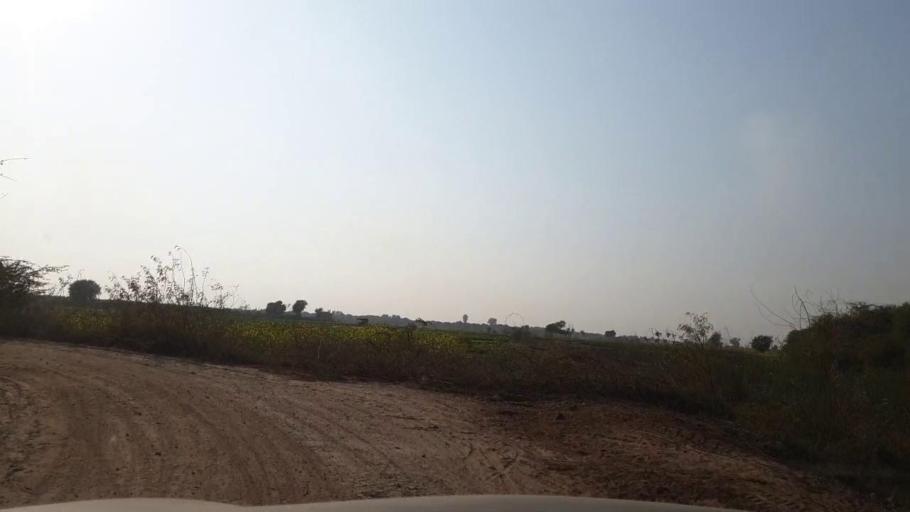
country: PK
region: Sindh
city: Tando Allahyar
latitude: 25.5812
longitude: 68.7643
